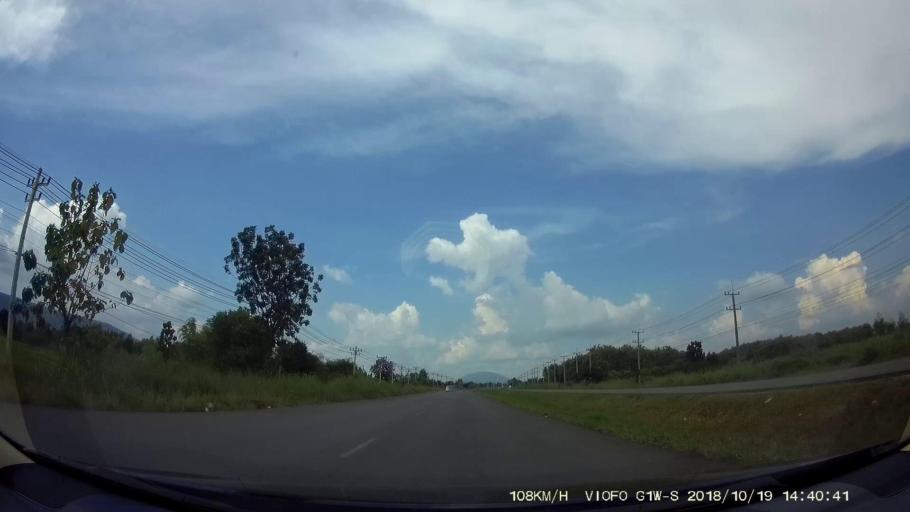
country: TH
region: Chaiyaphum
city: Phu Khiao
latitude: 16.2447
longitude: 102.1961
